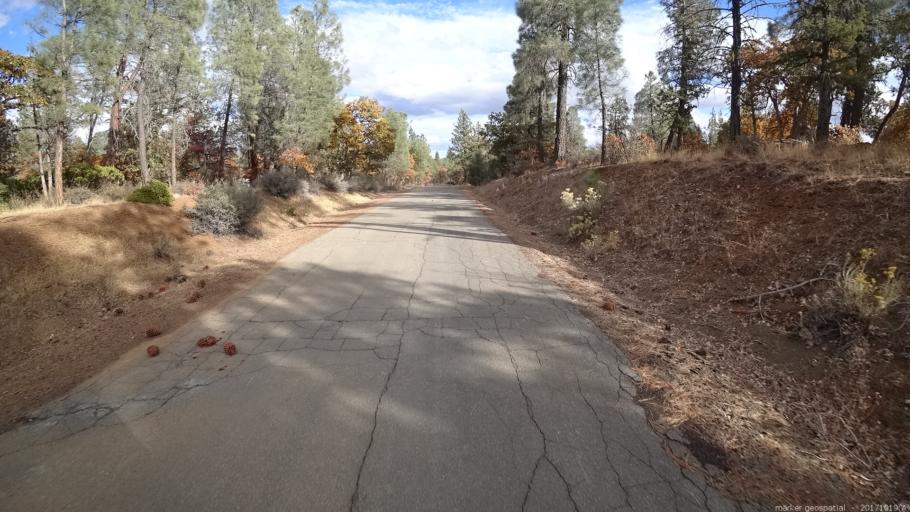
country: US
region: California
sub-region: Shasta County
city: Burney
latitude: 40.9589
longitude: -121.4418
